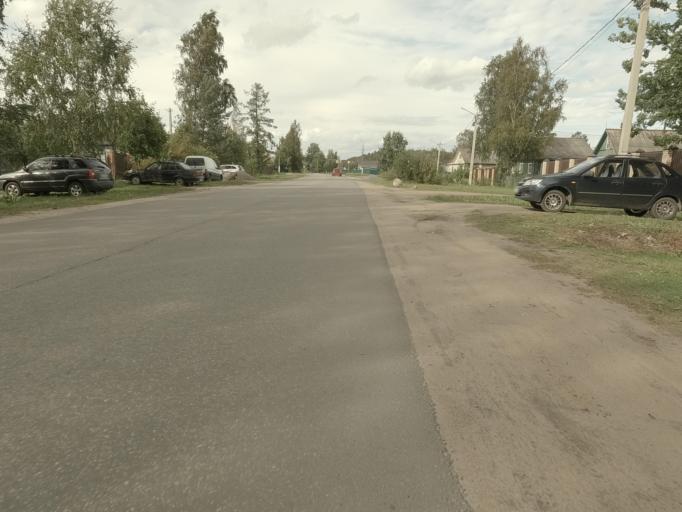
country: RU
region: Leningrad
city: Mga
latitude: 59.7560
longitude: 31.0765
